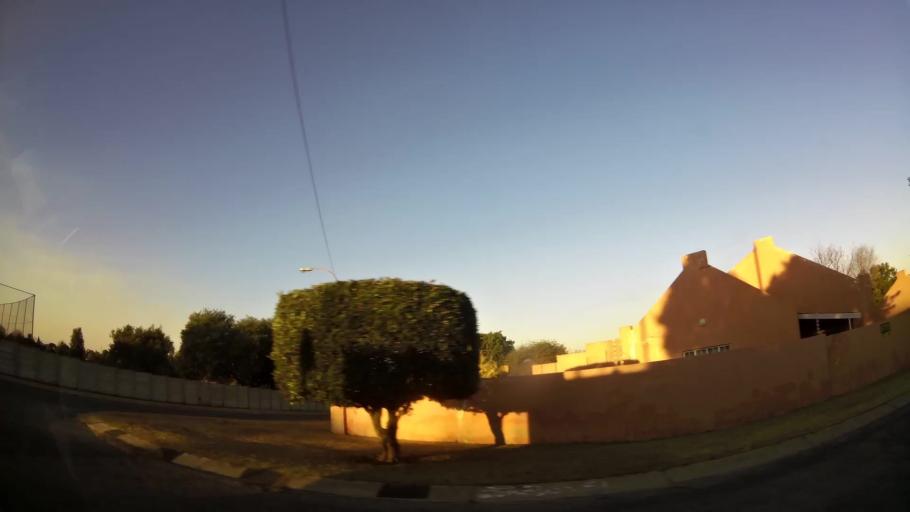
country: ZA
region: Gauteng
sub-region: City of Johannesburg Metropolitan Municipality
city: Roodepoort
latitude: -26.1503
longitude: 27.8956
